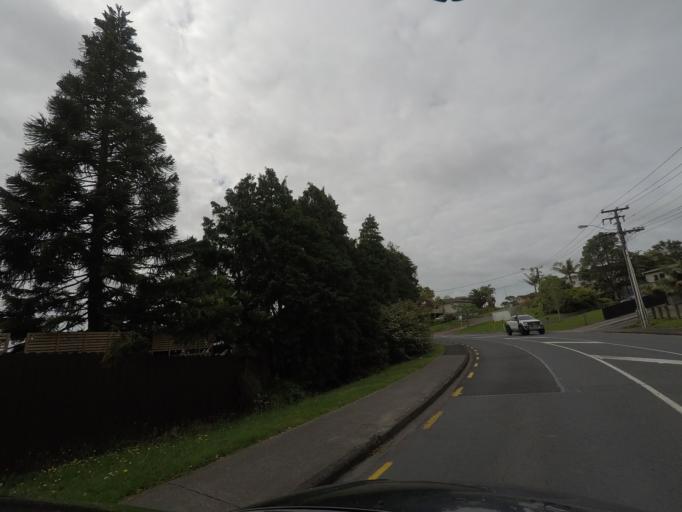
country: NZ
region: Auckland
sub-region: Auckland
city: Rosebank
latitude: -36.8523
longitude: 174.6100
